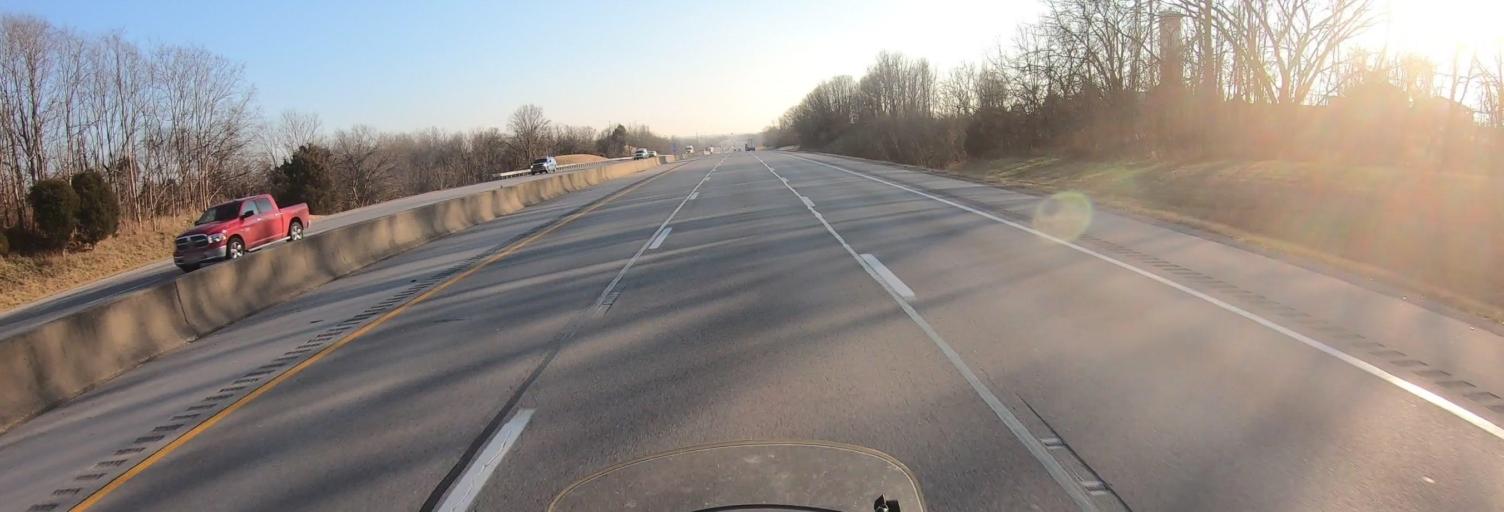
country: US
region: Kentucky
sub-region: Scott County
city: Georgetown
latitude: 38.3120
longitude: -84.5594
